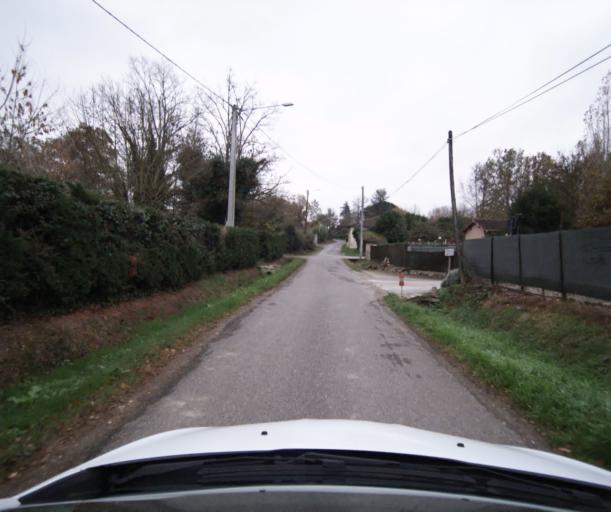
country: FR
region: Midi-Pyrenees
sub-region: Departement du Tarn-et-Garonne
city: Moissac
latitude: 44.0784
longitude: 1.1038
